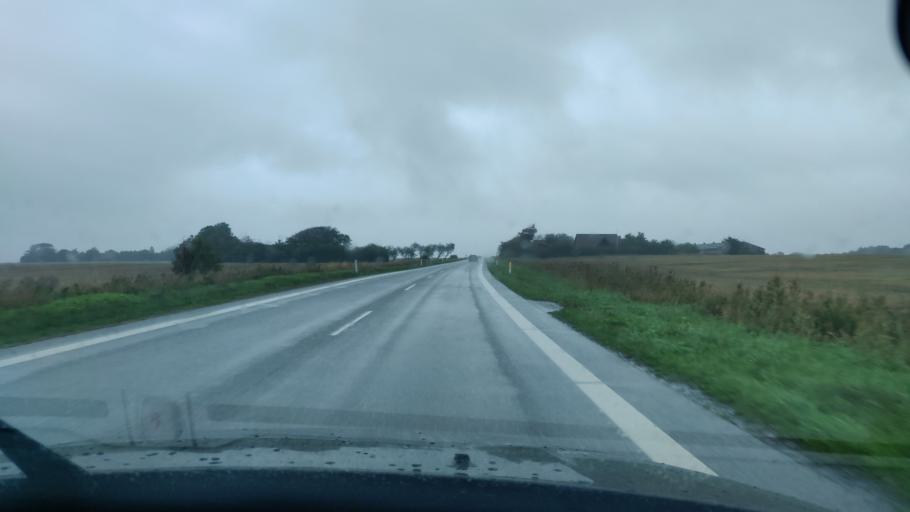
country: DK
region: North Denmark
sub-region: Thisted Kommune
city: Hurup
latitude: 56.8566
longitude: 8.5466
